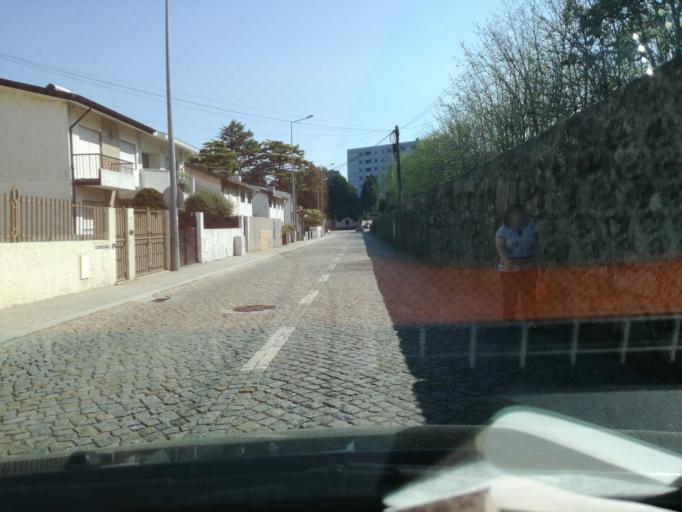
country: PT
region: Porto
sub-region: Maia
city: Maia
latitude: 41.2365
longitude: -8.6302
